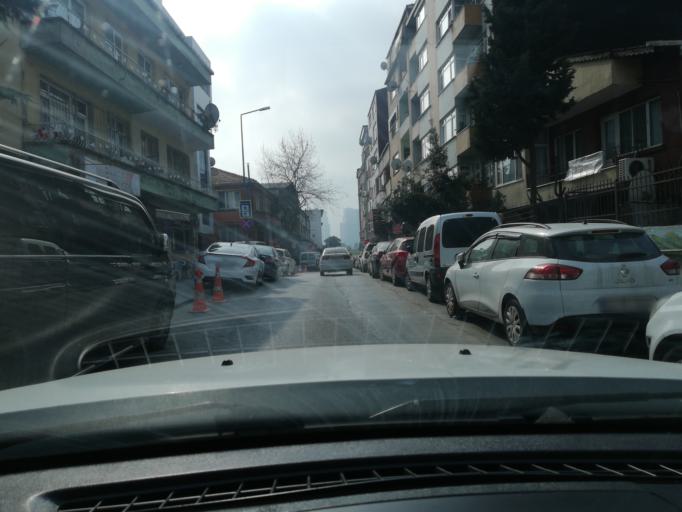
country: TR
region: Istanbul
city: Sisli
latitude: 41.0699
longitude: 28.9775
